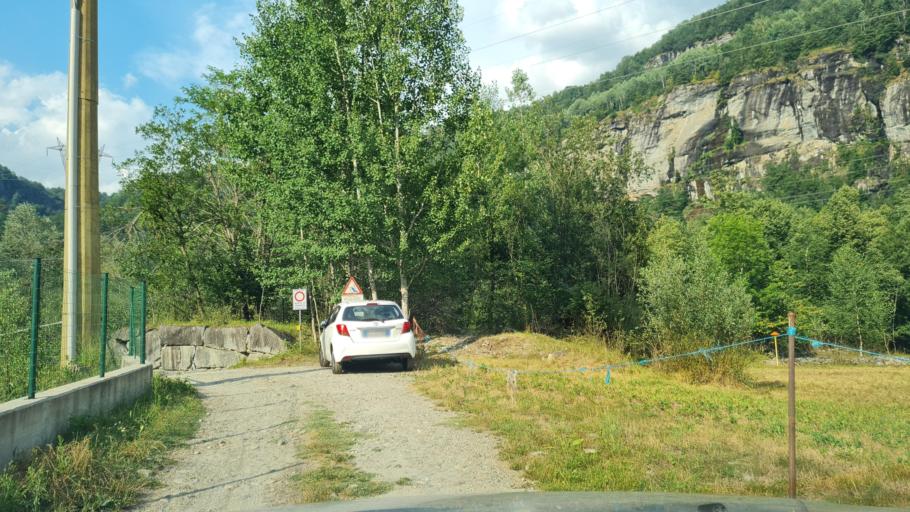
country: IT
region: Piedmont
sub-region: Provincia Verbano-Cusio-Ossola
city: Baceno
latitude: 46.2503
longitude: 8.3287
